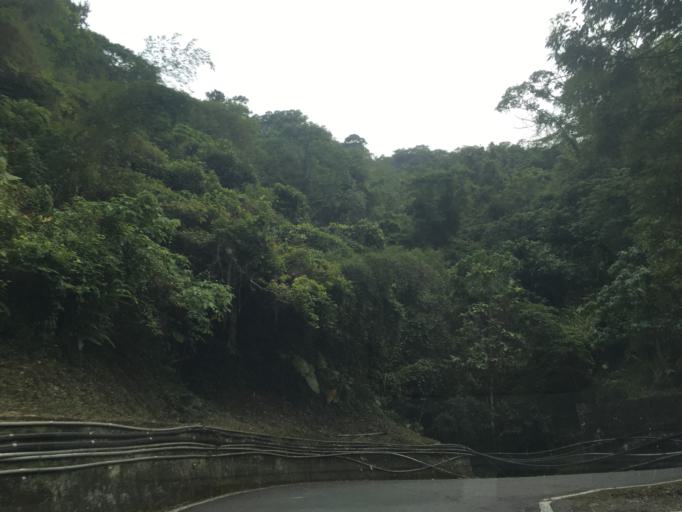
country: TW
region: Taiwan
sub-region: Nantou
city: Puli
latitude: 23.9468
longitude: 120.8553
